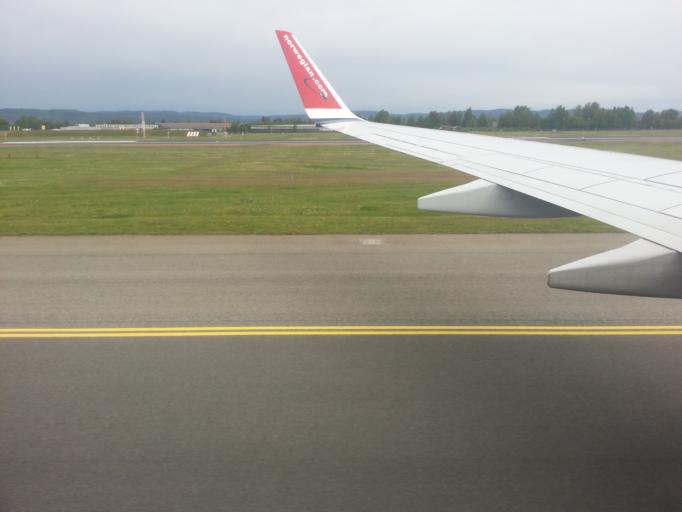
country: NO
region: Akershus
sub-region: Nannestad
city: Teigebyen
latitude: 60.1878
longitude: 11.0795
